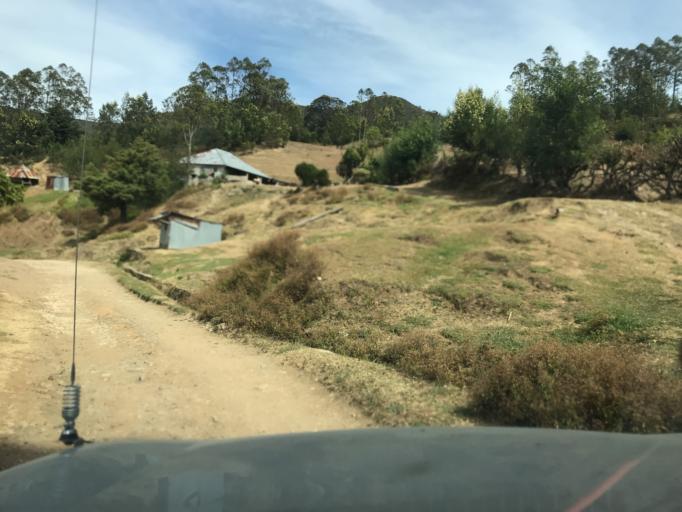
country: TL
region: Ainaro
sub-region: Ainaro
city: Ainaro
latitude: -8.8823
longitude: 125.5313
